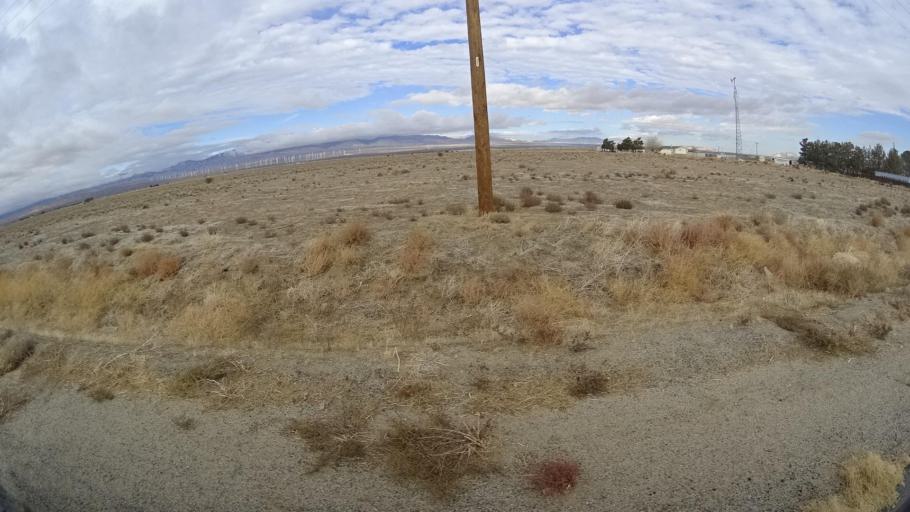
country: US
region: California
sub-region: Los Angeles County
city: Green Valley
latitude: 34.8192
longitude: -118.3834
